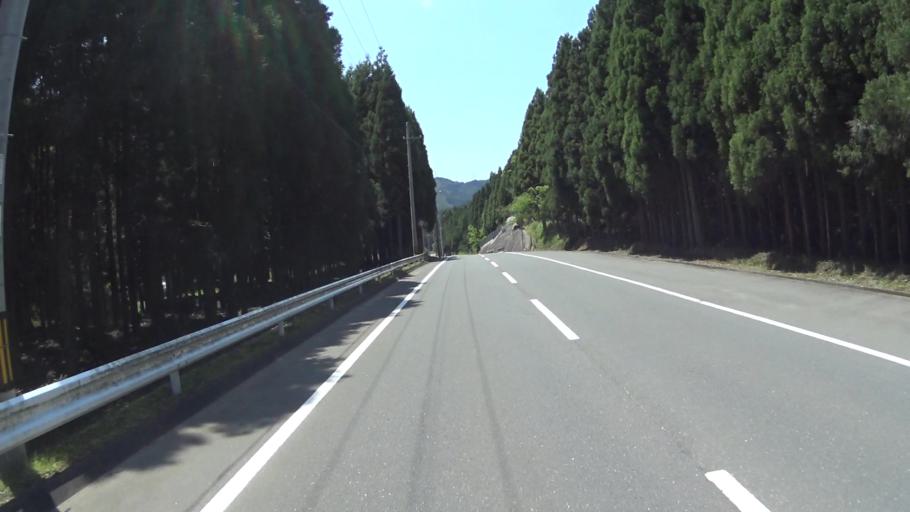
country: JP
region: Kyoto
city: Kameoka
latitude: 35.1476
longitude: 135.6162
